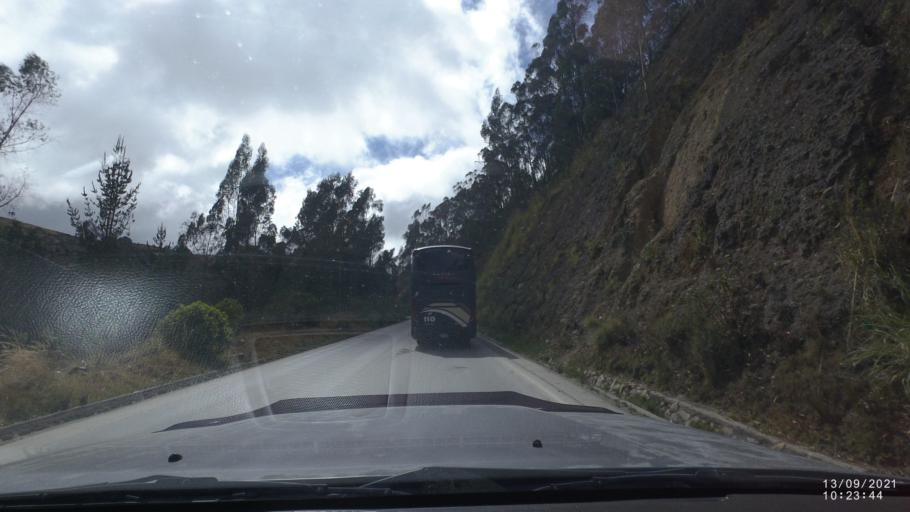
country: BO
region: Cochabamba
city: Colomi
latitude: -17.3178
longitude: -65.8656
